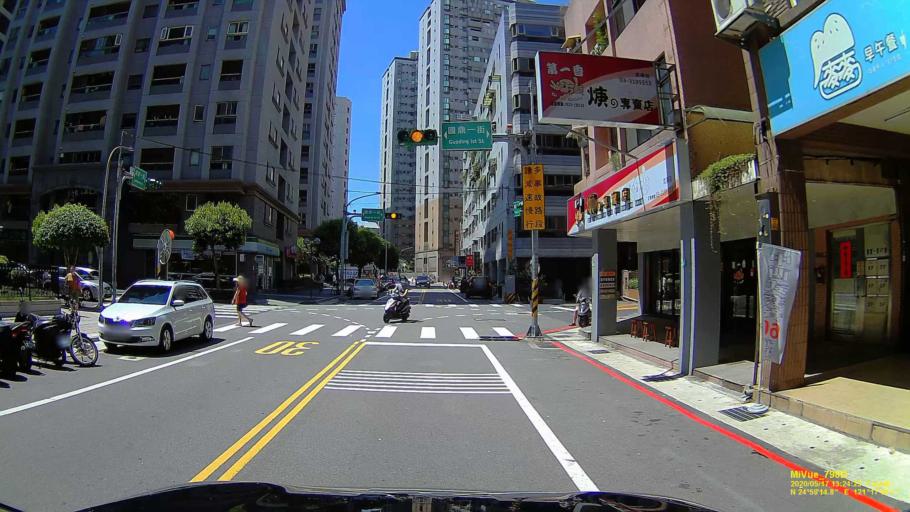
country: TW
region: Taiwan
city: Taoyuan City
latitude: 24.9875
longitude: 121.2880
